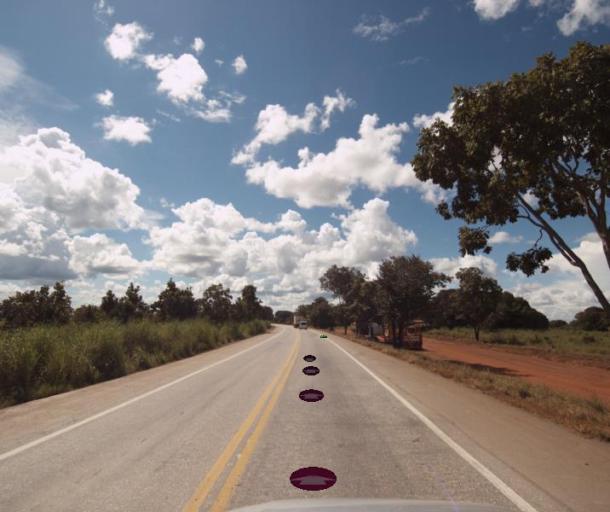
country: BR
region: Goias
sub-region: Porangatu
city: Porangatu
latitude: -13.5805
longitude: -49.0415
